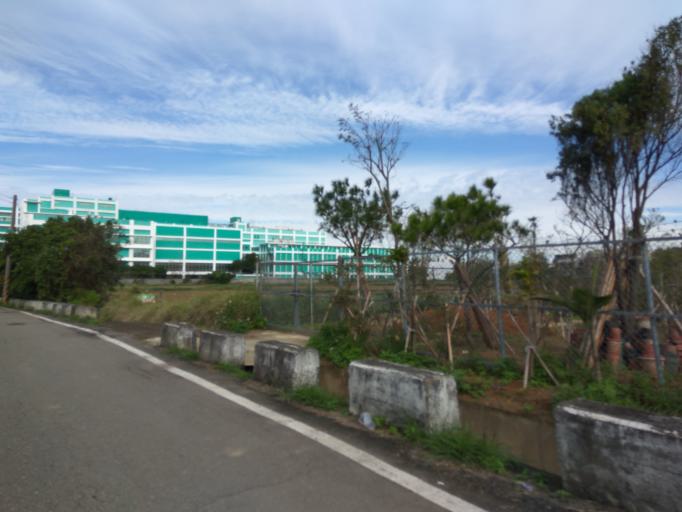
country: TW
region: Taiwan
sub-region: Hsinchu
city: Zhubei
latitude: 24.9910
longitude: 121.1008
